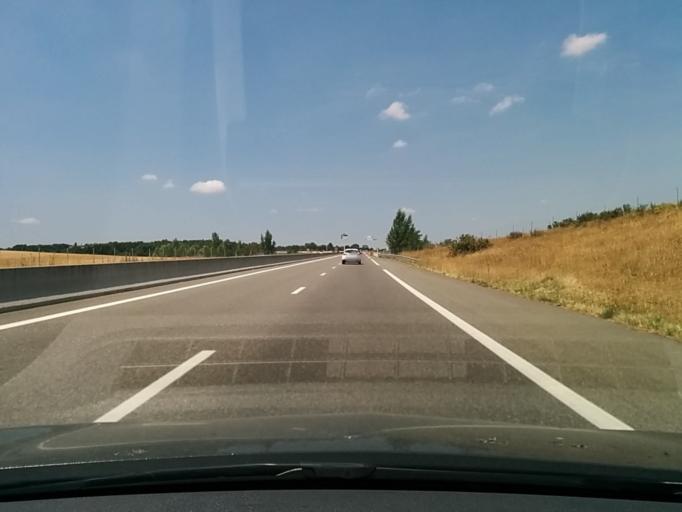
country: FR
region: Midi-Pyrenees
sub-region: Departement du Gers
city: Pujaudran
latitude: 43.5861
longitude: 1.1763
